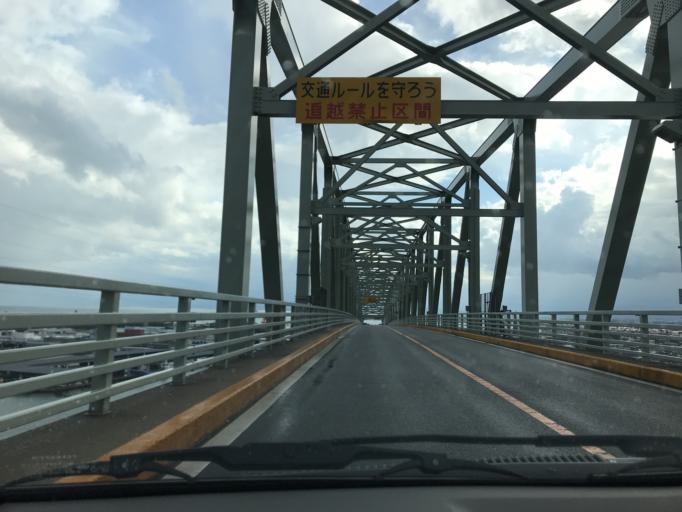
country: JP
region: Shimane
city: Sakaiminato
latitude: 35.5503
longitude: 133.2441
